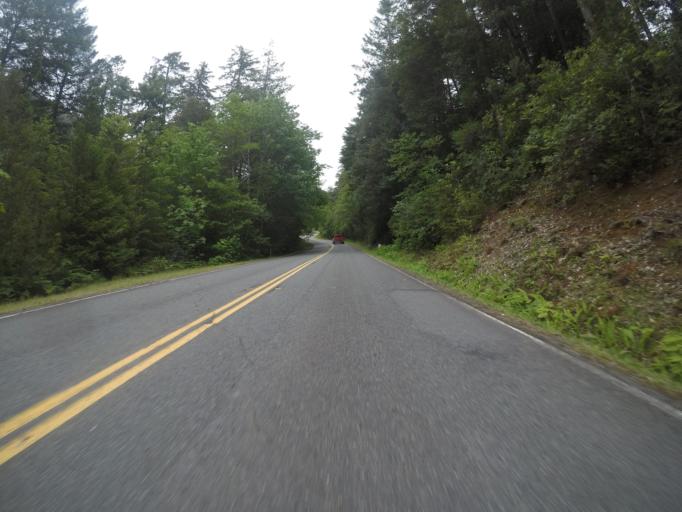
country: US
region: California
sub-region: Del Norte County
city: Bertsch-Oceanview
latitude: 41.7264
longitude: -123.9604
